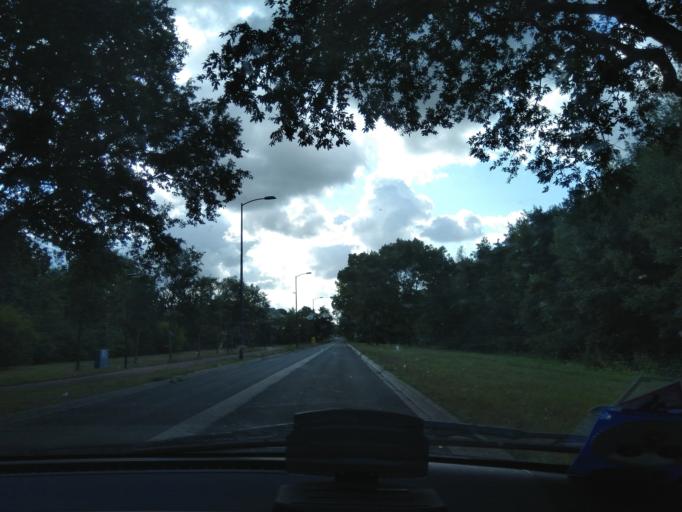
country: NL
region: North Brabant
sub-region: Gemeente Oosterhout
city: Oosterhout
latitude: 51.6205
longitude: 4.8516
